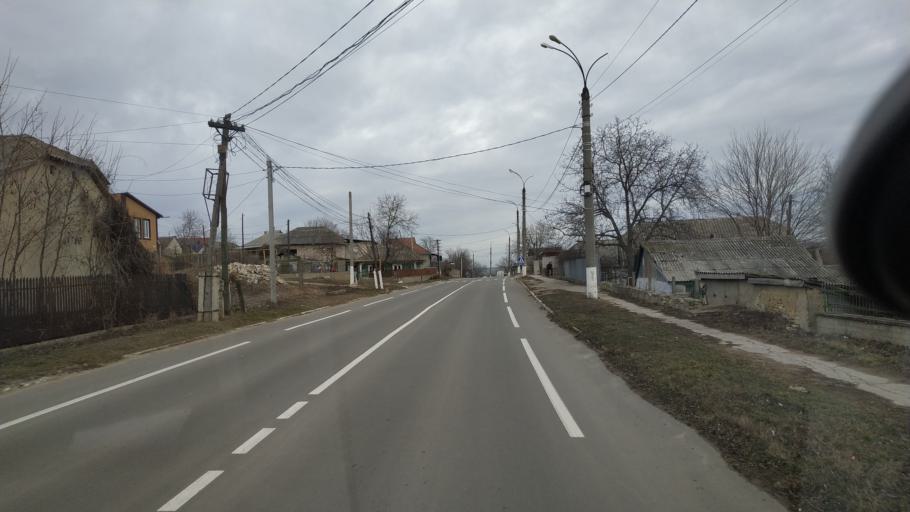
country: MD
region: Criuleni
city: Criuleni
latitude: 47.2188
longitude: 29.1631
